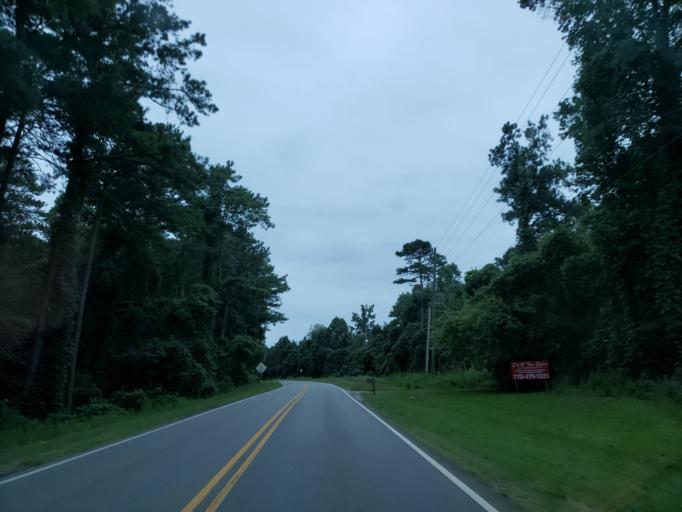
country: US
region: Georgia
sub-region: Cherokee County
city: Canton
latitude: 34.2883
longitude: -84.4541
